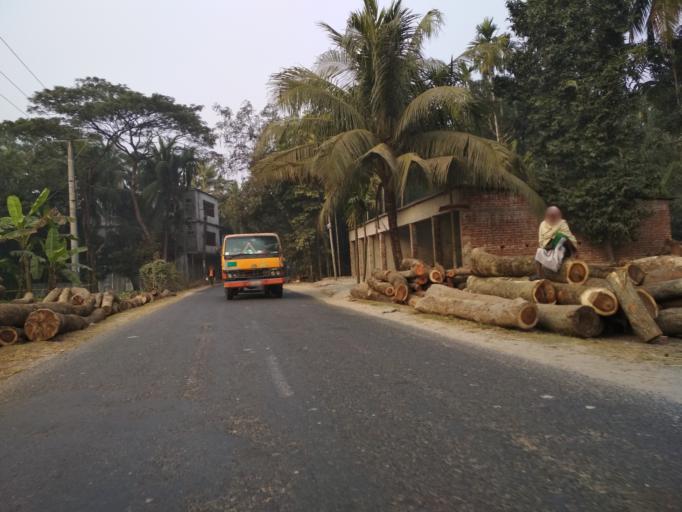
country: BD
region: Chittagong
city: Lakshmipur
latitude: 22.9190
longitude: 90.8373
